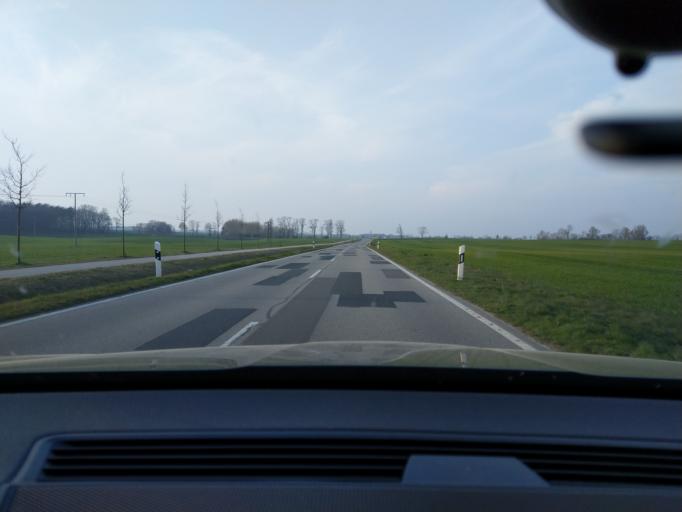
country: DE
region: Mecklenburg-Vorpommern
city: Prohn
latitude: 54.3442
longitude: 13.0301
